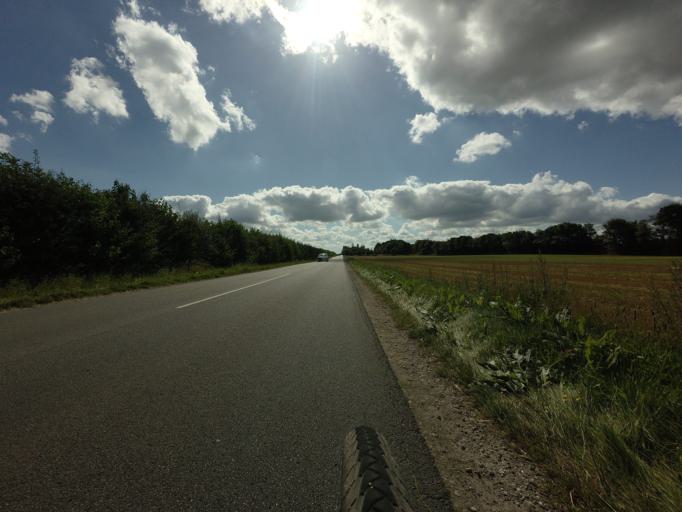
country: DK
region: Central Jutland
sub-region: Ikast-Brande Kommune
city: Brande
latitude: 55.9774
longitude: 9.1444
